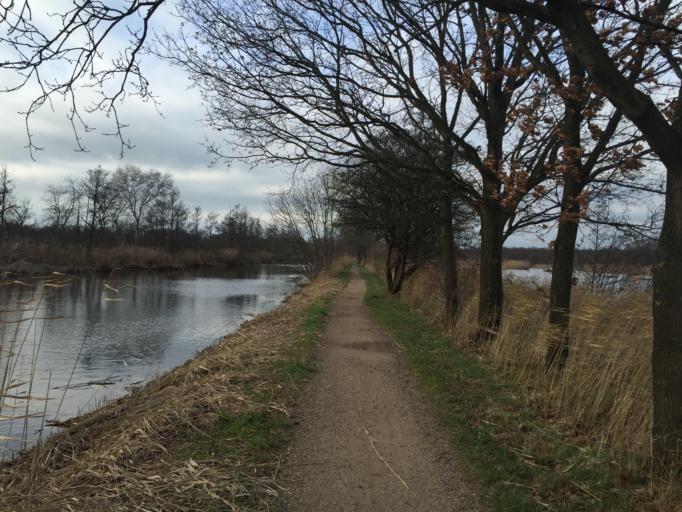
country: NL
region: North Holland
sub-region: Gemeente Wijdemeren
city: Kortenhoef
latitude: 52.2641
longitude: 5.0748
